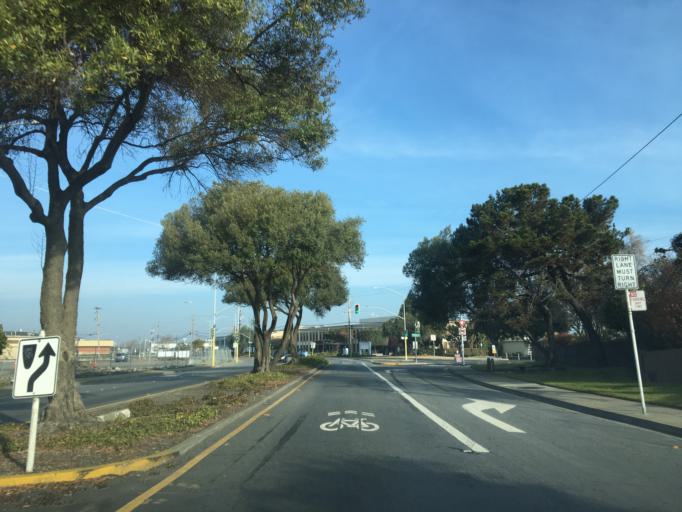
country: US
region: California
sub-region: Alameda County
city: San Leandro
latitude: 37.6996
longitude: -122.1657
